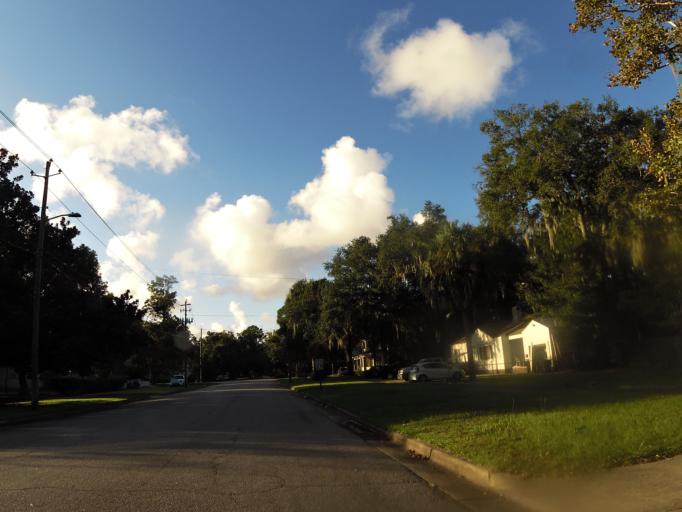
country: US
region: Georgia
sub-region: Glynn County
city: Brunswick
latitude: 31.1363
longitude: -81.4885
